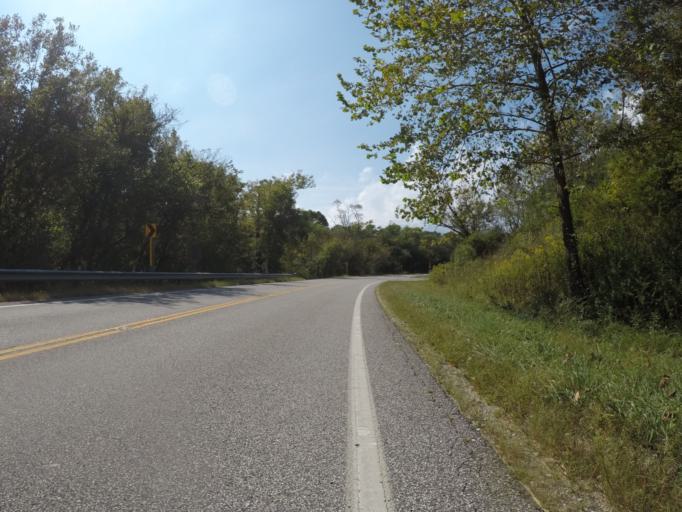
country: US
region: West Virginia
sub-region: Cabell County
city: Lesage
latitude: 38.5178
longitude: -82.3883
